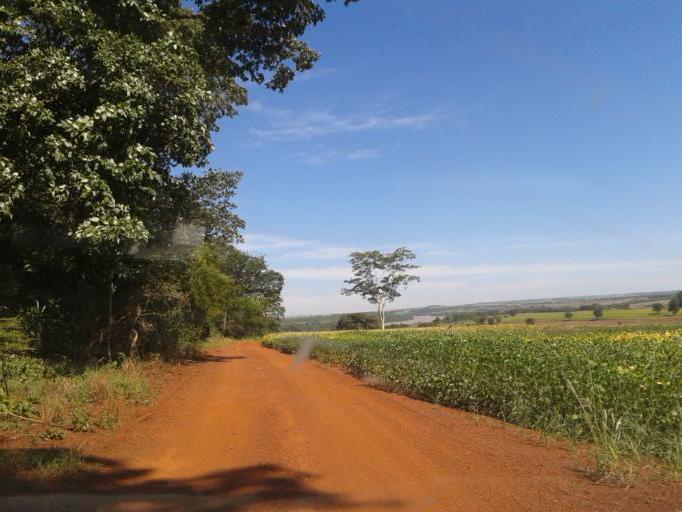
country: BR
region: Minas Gerais
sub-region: Capinopolis
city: Capinopolis
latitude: -18.6123
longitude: -49.6131
